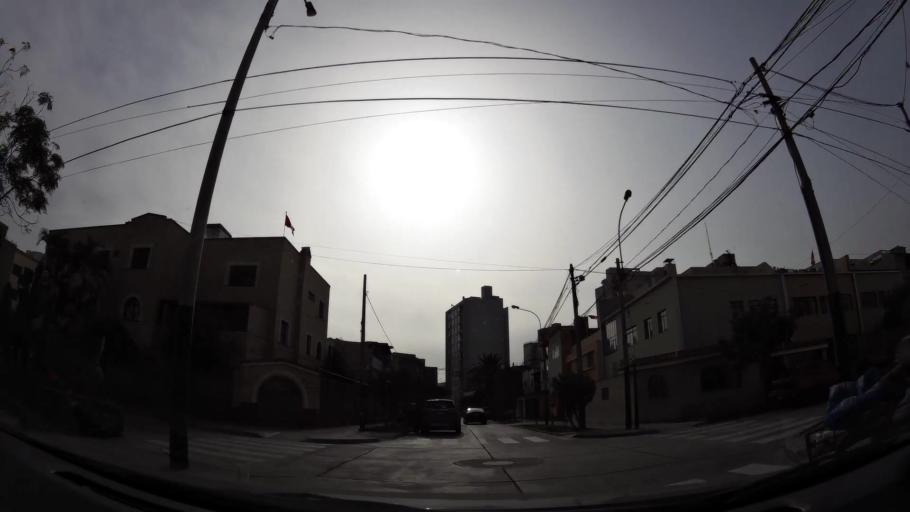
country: PE
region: Lima
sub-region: Lima
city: San Isidro
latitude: -12.0931
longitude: -77.0667
